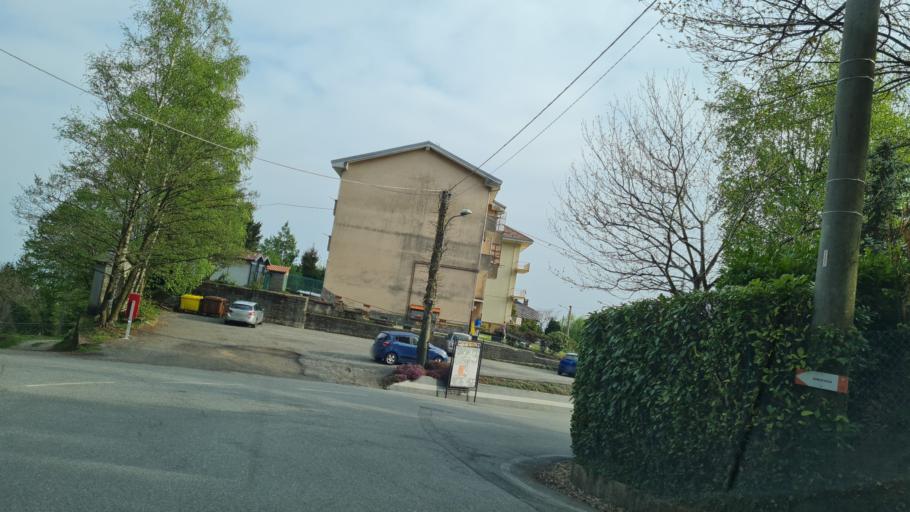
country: IT
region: Piedmont
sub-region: Provincia di Biella
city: Sordevolo
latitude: 45.5782
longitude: 7.9692
